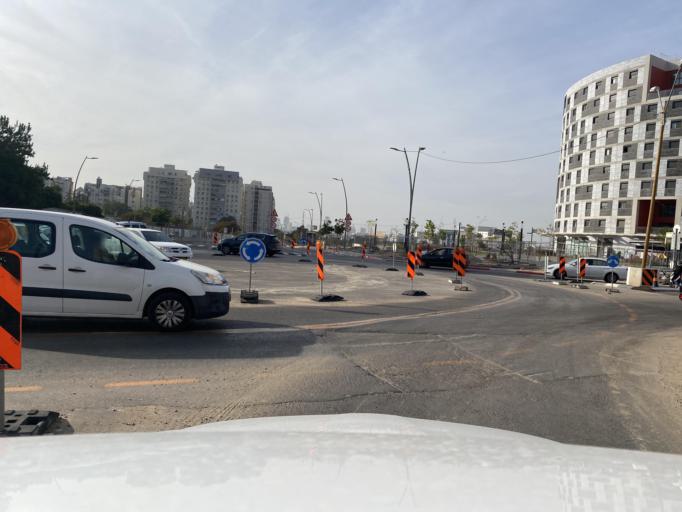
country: IL
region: Tel Aviv
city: Giv`at Shemu'el
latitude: 32.0702
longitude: 34.8506
